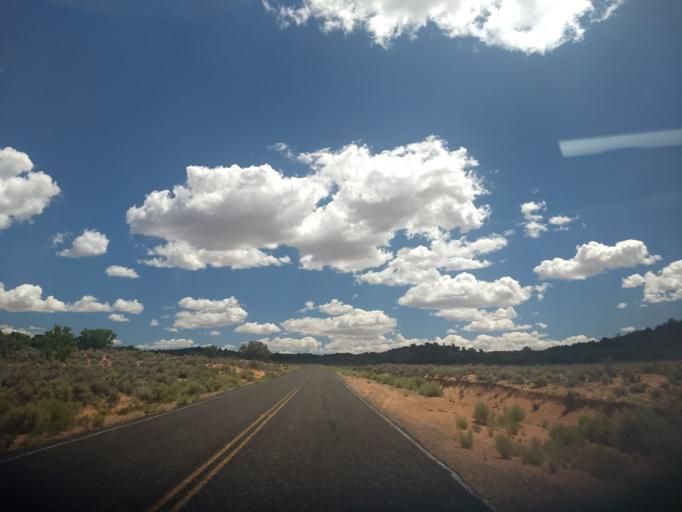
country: US
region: Utah
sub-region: Kane County
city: Kanab
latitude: 37.1357
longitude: -112.6761
